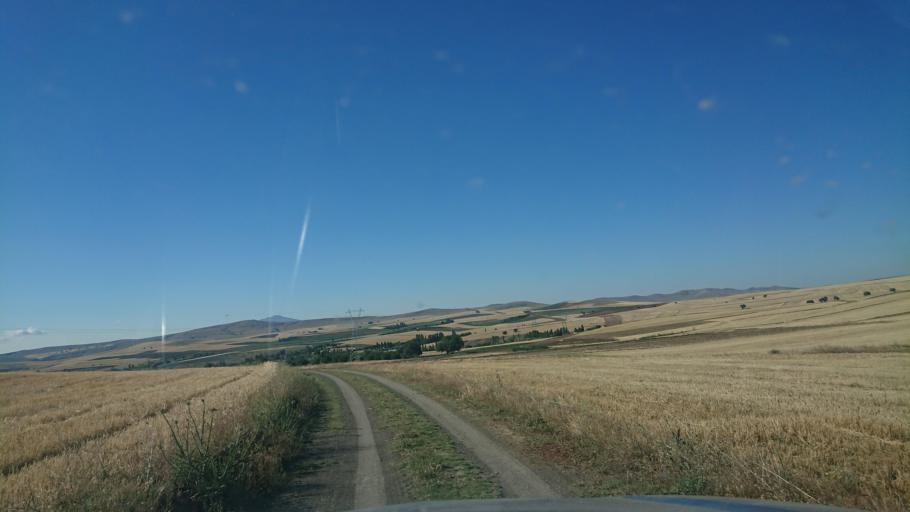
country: TR
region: Aksaray
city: Agacoren
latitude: 38.8307
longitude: 33.9427
